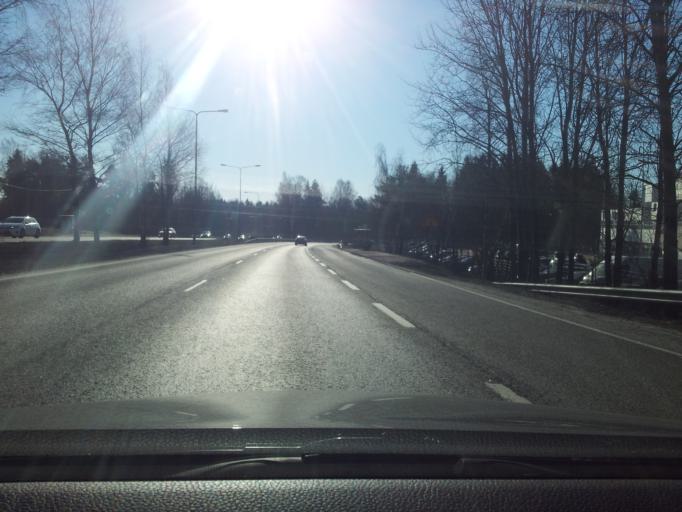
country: FI
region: Uusimaa
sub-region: Helsinki
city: Vantaa
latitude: 60.2252
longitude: 25.0781
